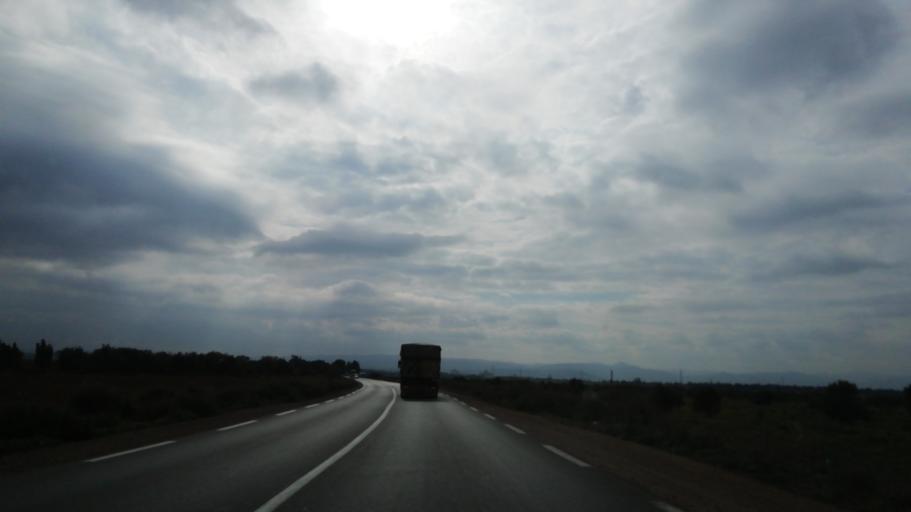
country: DZ
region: Oran
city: Sidi ech Chahmi
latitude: 35.5885
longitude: -0.4536
